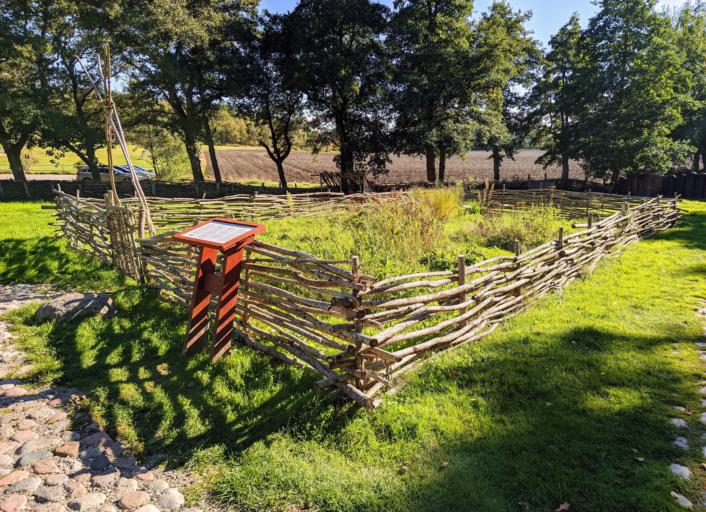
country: SE
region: Vaestra Goetaland
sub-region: Tanums Kommun
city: Tanumshede
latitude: 58.7019
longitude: 11.3425
